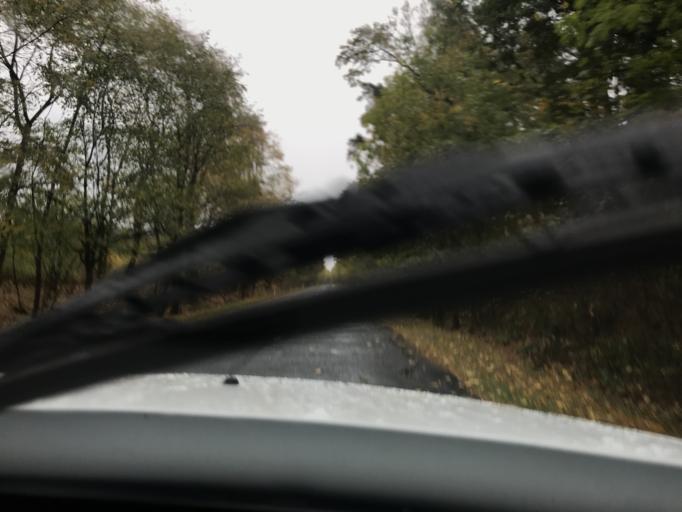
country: PL
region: West Pomeranian Voivodeship
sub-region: Powiat gryfinski
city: Mieszkowice
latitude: 52.7847
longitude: 14.4315
